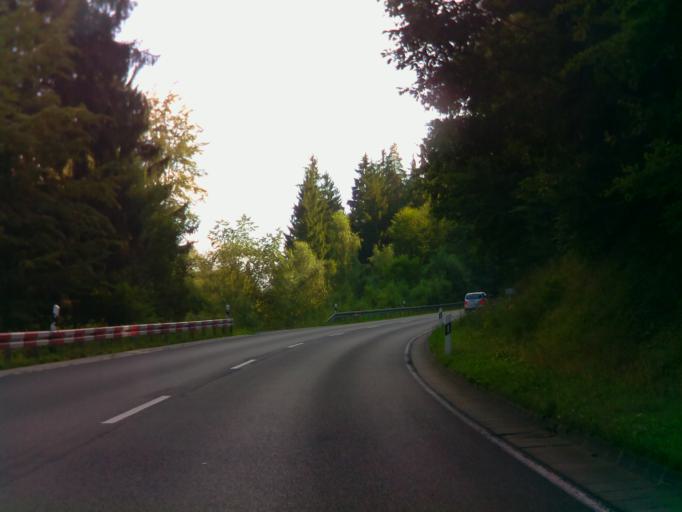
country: DE
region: Bavaria
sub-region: Regierungsbezirk Unterfranken
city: Riedenberg
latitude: 50.3093
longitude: 9.8450
